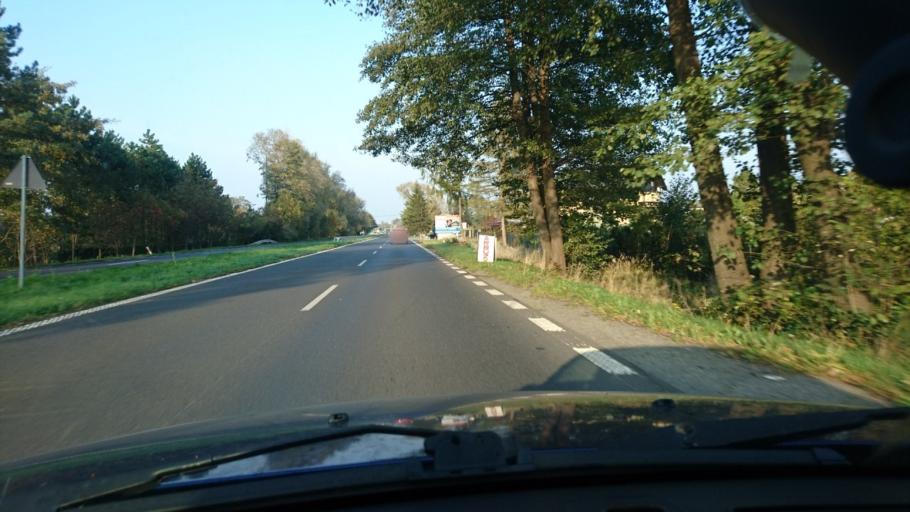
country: PL
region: Silesian Voivodeship
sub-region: Powiat cieszynski
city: Ustron
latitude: 49.7534
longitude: 18.7978
